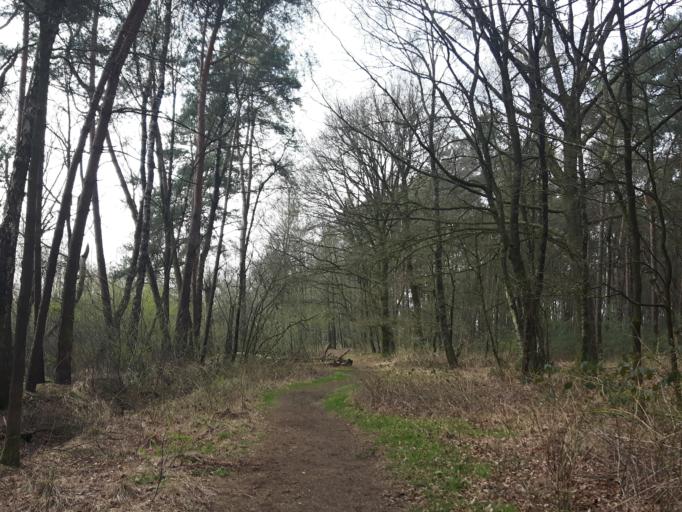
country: NL
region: Overijssel
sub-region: Gemeente Haaksbergen
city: Haaksbergen
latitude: 52.1582
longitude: 6.8069
